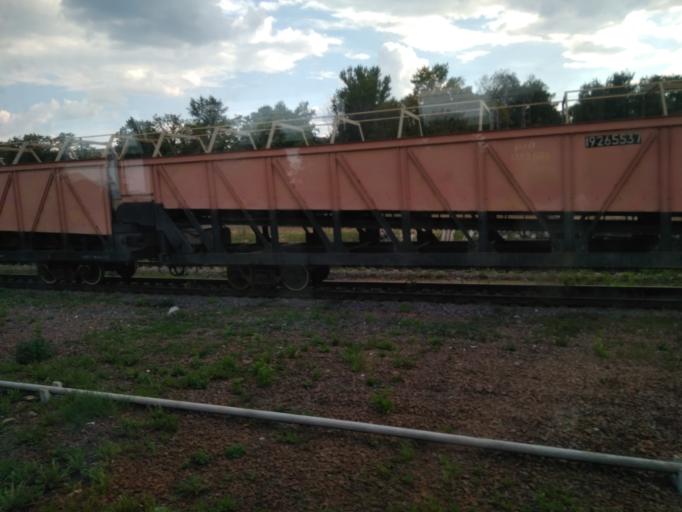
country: RU
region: Moskovskaya
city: Tomilino
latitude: 55.6642
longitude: 37.9321
